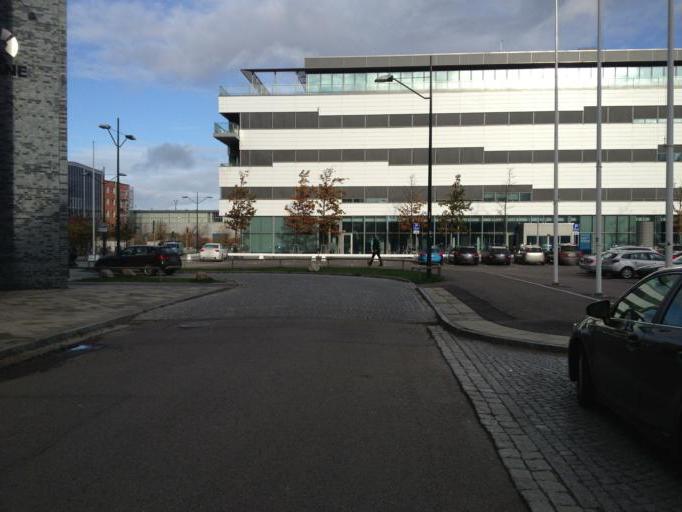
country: SE
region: Skane
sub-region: Malmo
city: Malmoe
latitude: 55.6144
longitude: 12.9887
